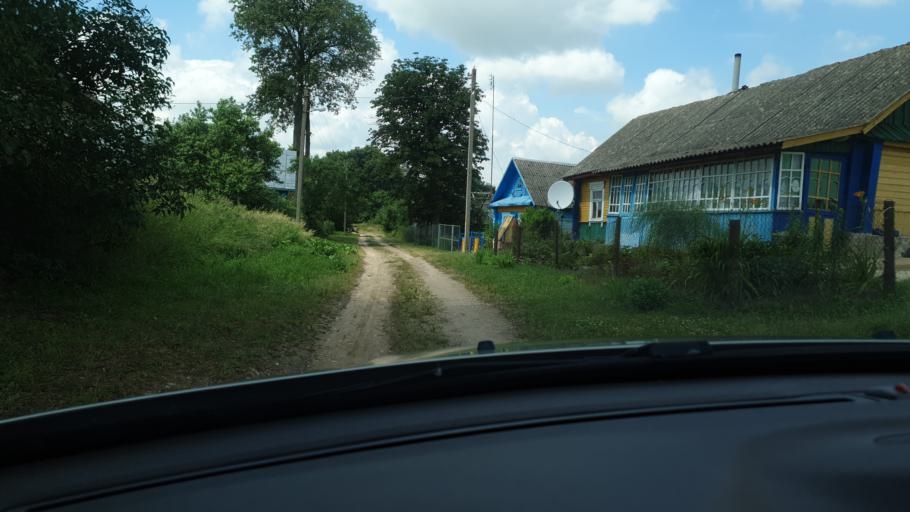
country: BY
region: Grodnenskaya
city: Mir
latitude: 53.3859
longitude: 26.3579
